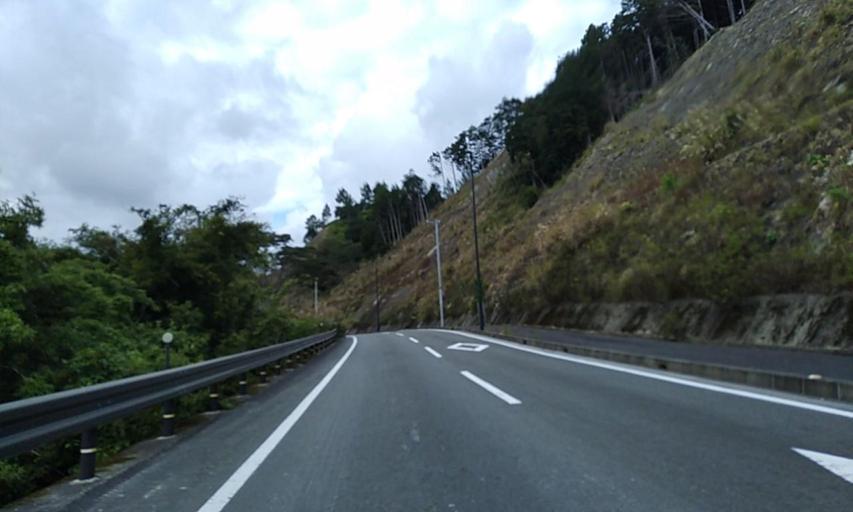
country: JP
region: Wakayama
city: Shingu
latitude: 33.5857
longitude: 135.9384
